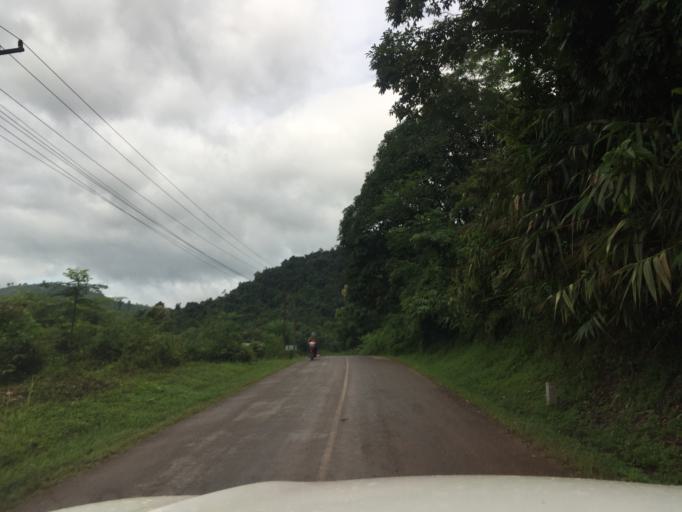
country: LA
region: Oudomxai
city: Muang La
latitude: 20.7911
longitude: 102.0826
